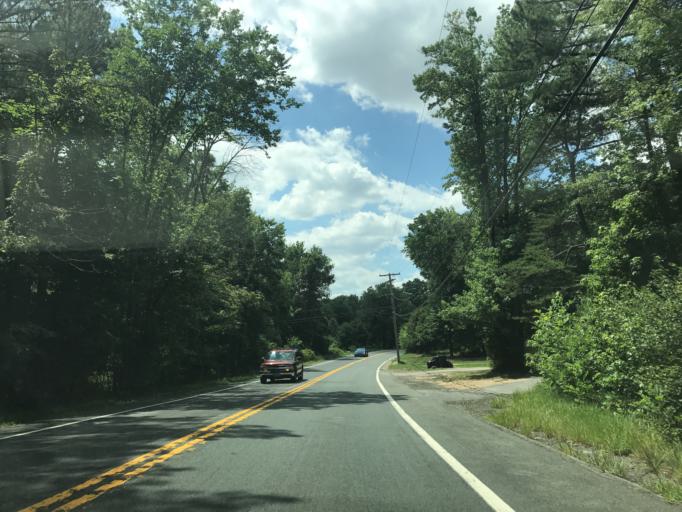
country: US
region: Maryland
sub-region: Prince George's County
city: South Laurel
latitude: 39.0463
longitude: -76.8255
